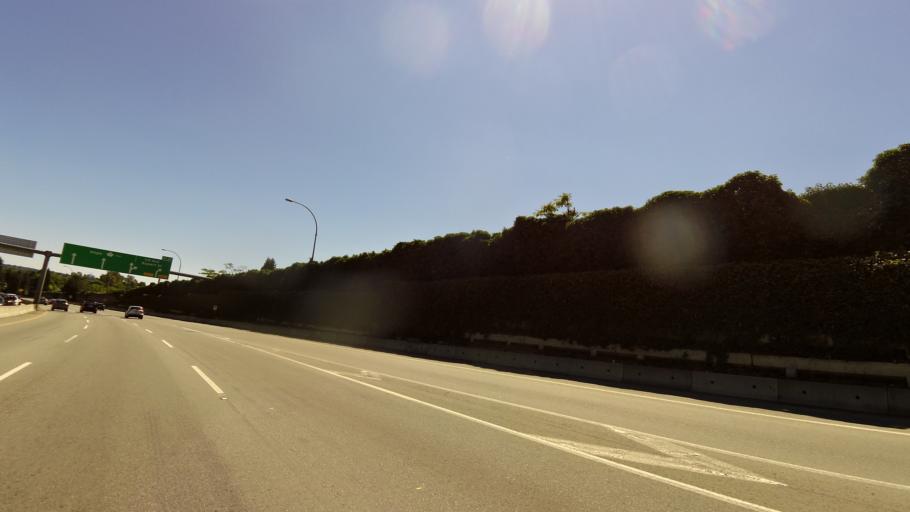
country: CA
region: British Columbia
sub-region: Fraser Valley Regional District
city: North Vancouver
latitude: 49.2769
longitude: -123.0312
